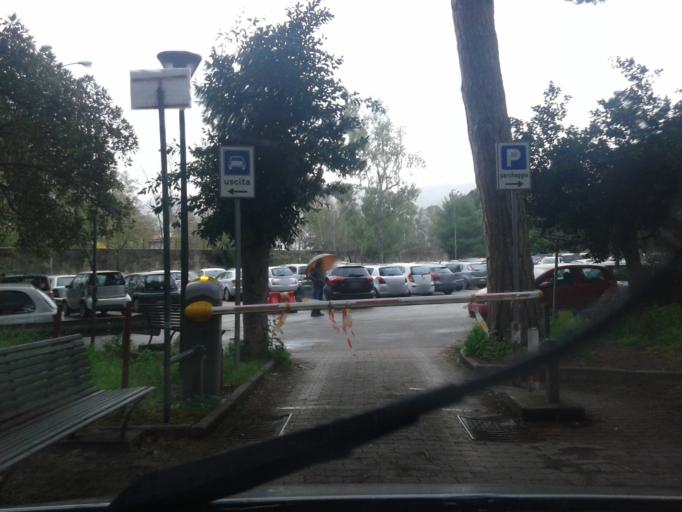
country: IT
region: Sicily
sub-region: Palermo
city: Monreale
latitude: 38.0932
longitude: 13.3116
